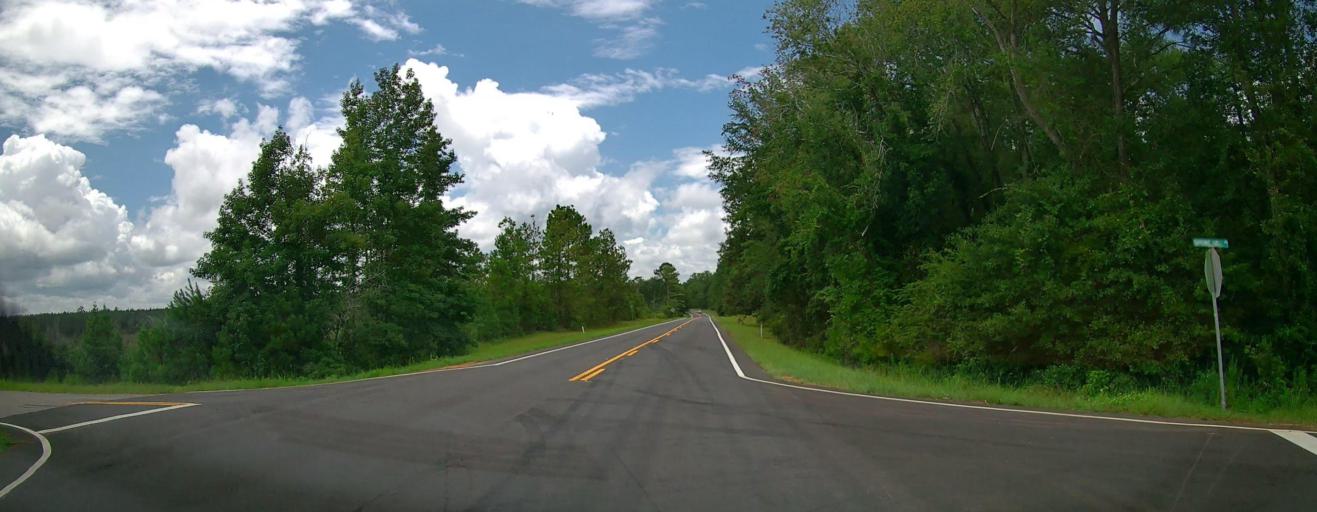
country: US
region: Georgia
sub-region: Dooly County
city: Vienna
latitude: 32.0736
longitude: -83.6272
